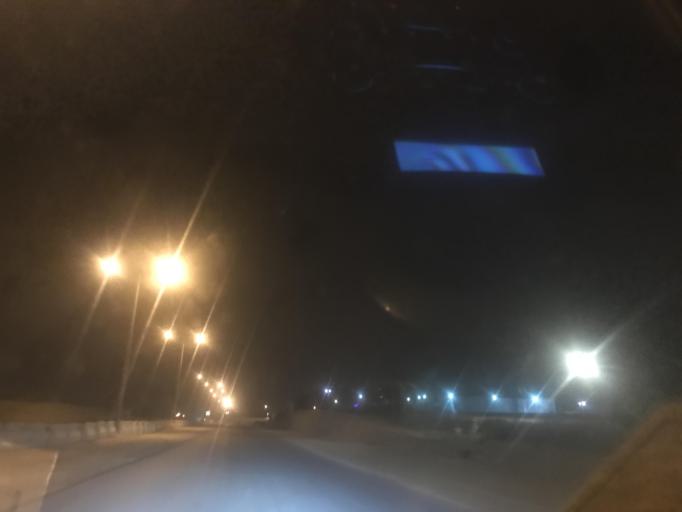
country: SA
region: Ar Riyad
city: Riyadh
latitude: 24.7596
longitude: 46.5895
